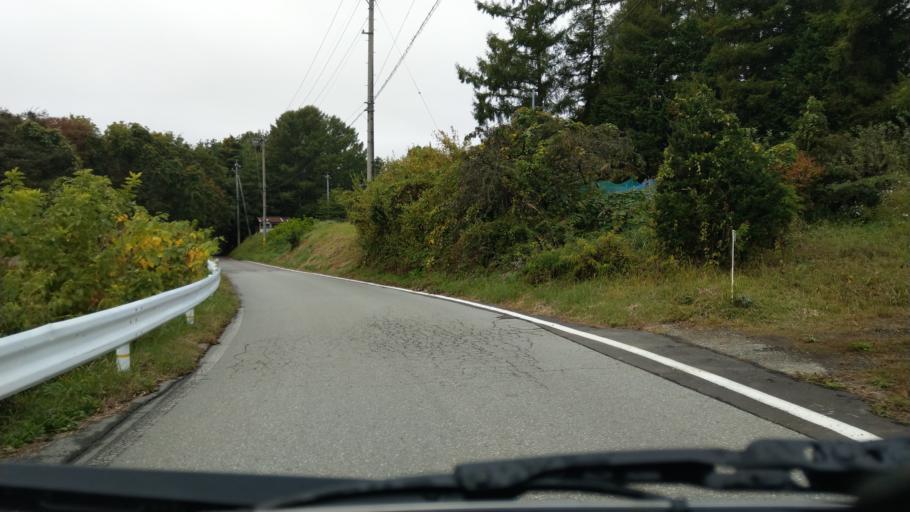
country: JP
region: Nagano
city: Komoro
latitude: 36.3548
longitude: 138.4382
